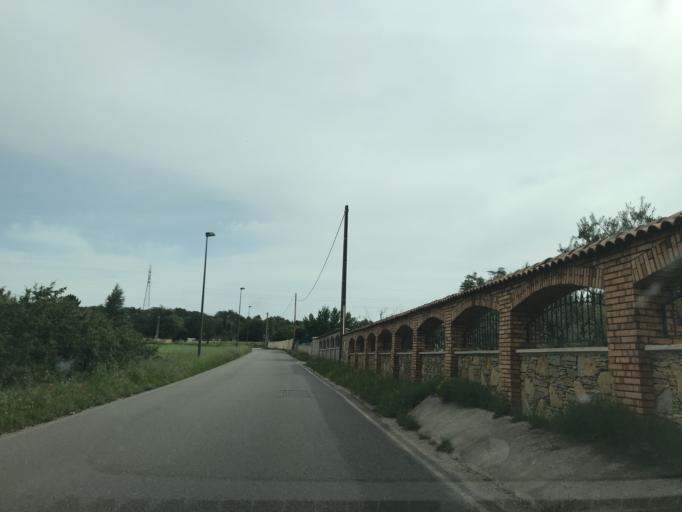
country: FR
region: Provence-Alpes-Cote d'Azur
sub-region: Departement du Var
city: Saint-Maximin-la-Sainte-Baume
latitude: 43.4587
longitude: 5.8752
